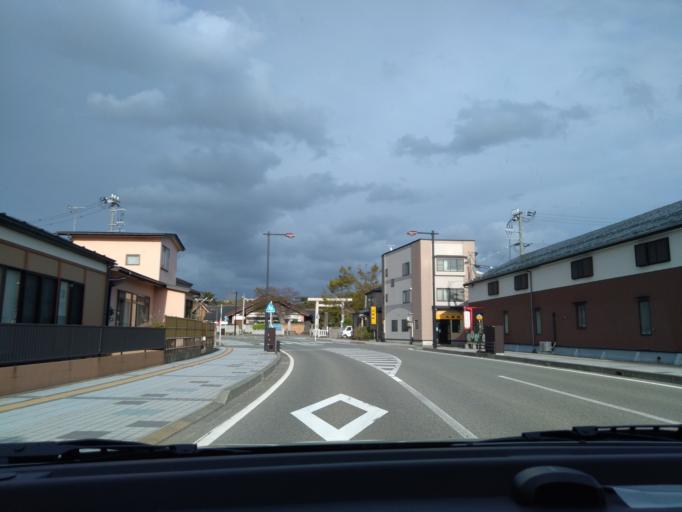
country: JP
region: Akita
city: Akita Shi
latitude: 39.7573
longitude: 140.0695
